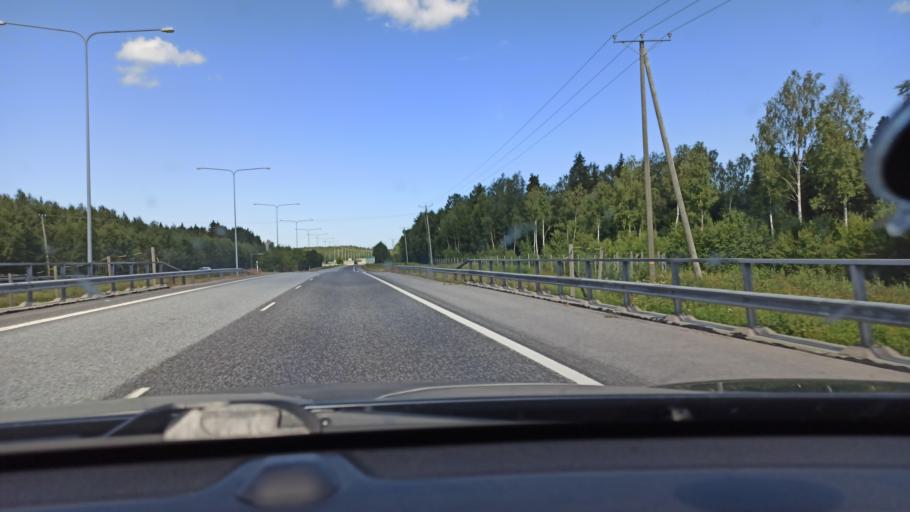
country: FI
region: Ostrobothnia
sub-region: Vaasa
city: Ristinummi
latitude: 63.0403
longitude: 21.7324
